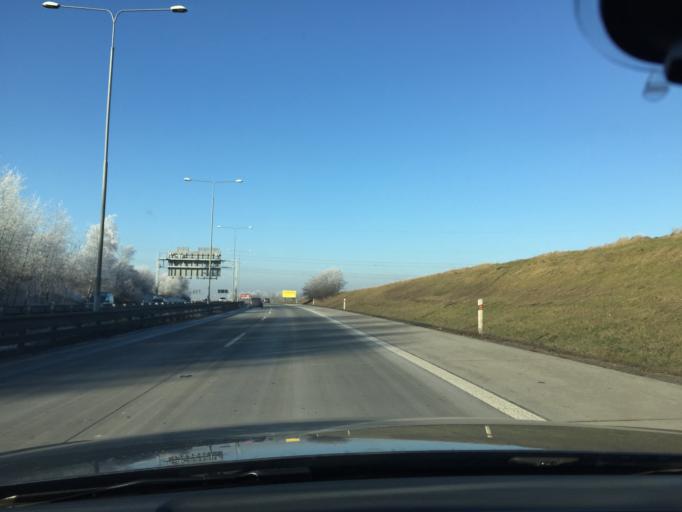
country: CZ
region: Central Bohemia
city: Cernosice
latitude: 50.0206
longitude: 14.3338
